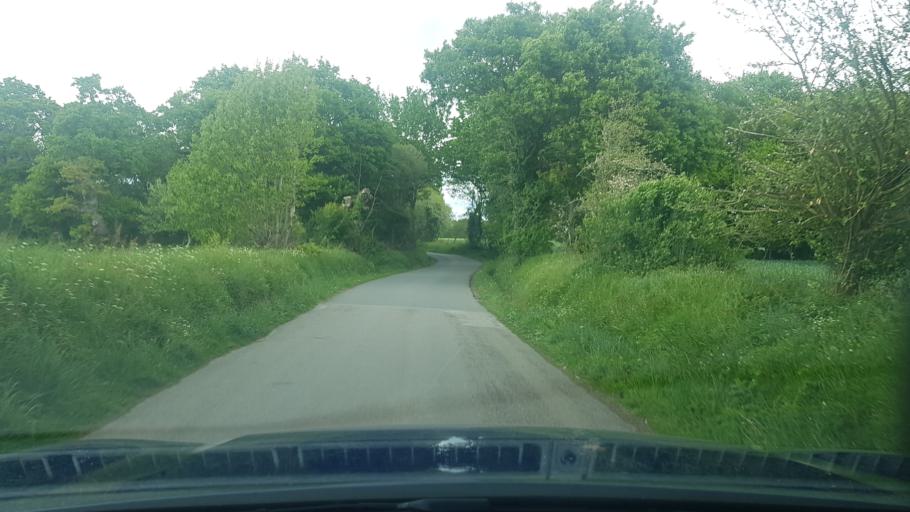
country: FR
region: Brittany
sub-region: Departement du Finistere
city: Quimperle
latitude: 47.8594
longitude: -3.5865
